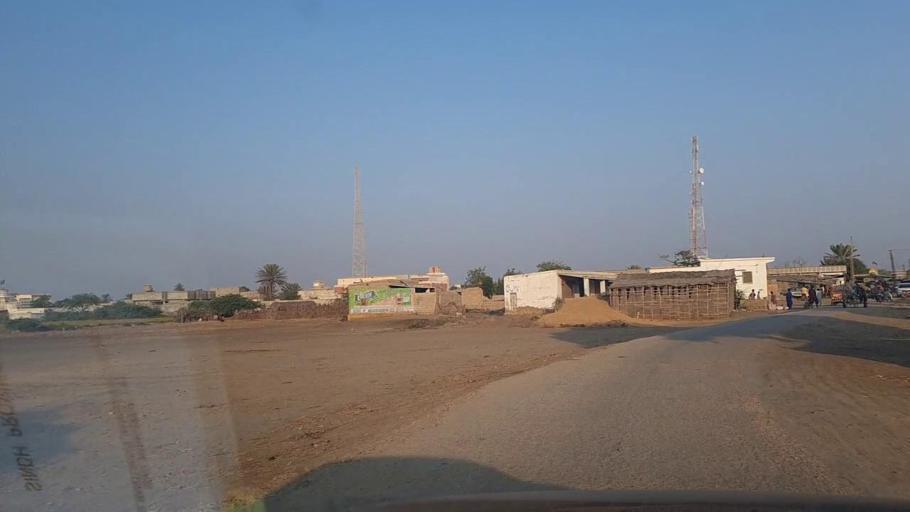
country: PK
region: Sindh
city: Keti Bandar
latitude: 24.3009
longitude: 67.6027
